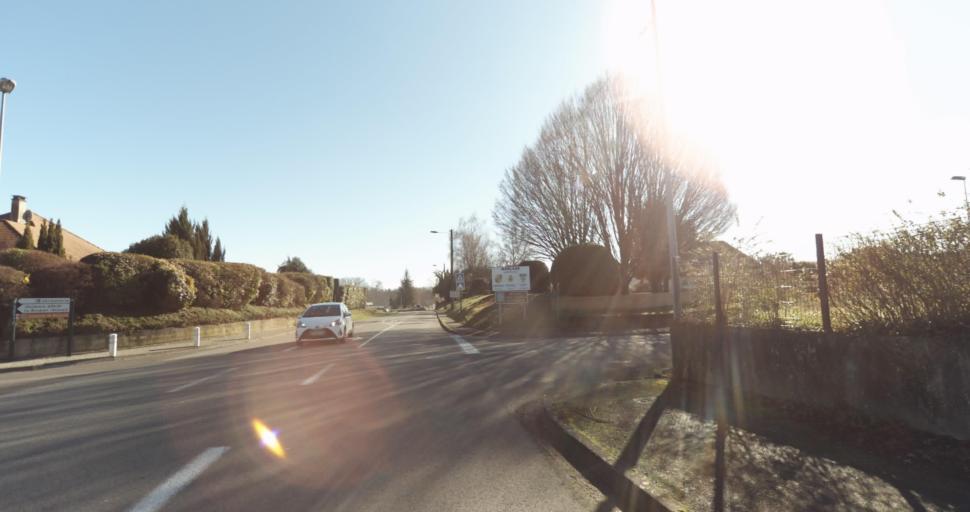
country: FR
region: Aquitaine
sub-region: Departement des Pyrenees-Atlantiques
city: Morlaas
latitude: 43.3520
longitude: -0.2656
